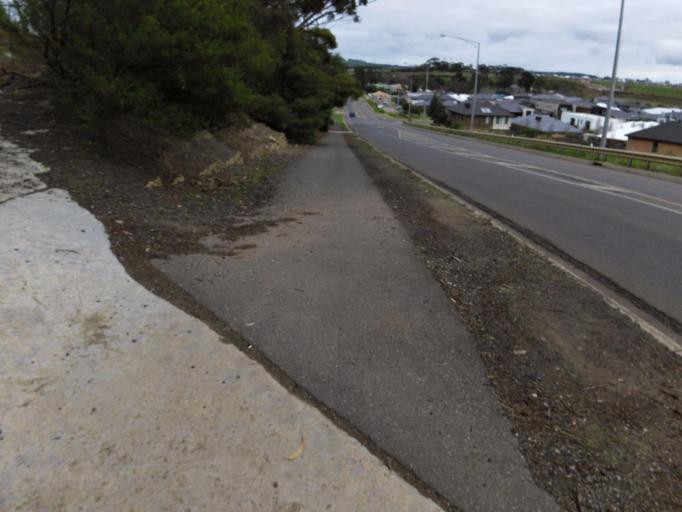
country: AU
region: Victoria
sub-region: Greater Geelong
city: Hamlyn Heights
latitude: -38.1389
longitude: 144.3153
